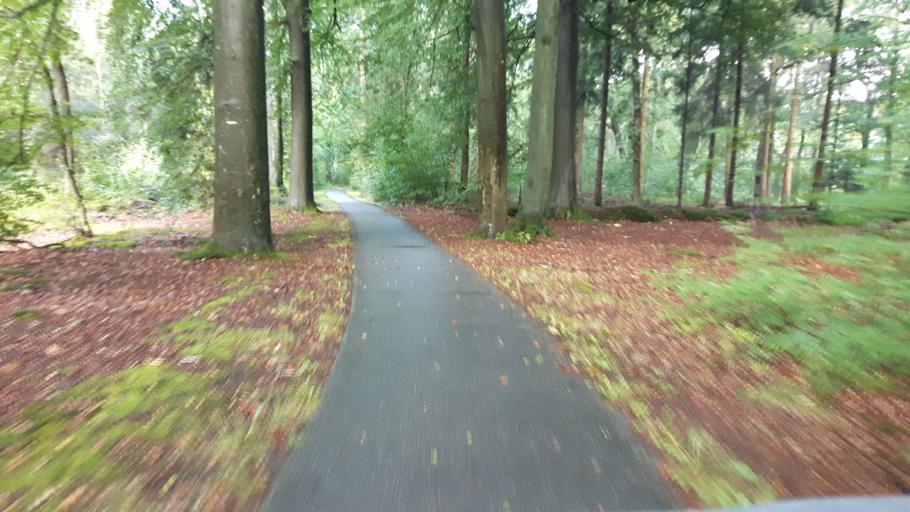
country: NL
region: Friesland
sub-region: Gemeente Smallingerland
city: Drachten
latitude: 53.0661
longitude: 6.1166
